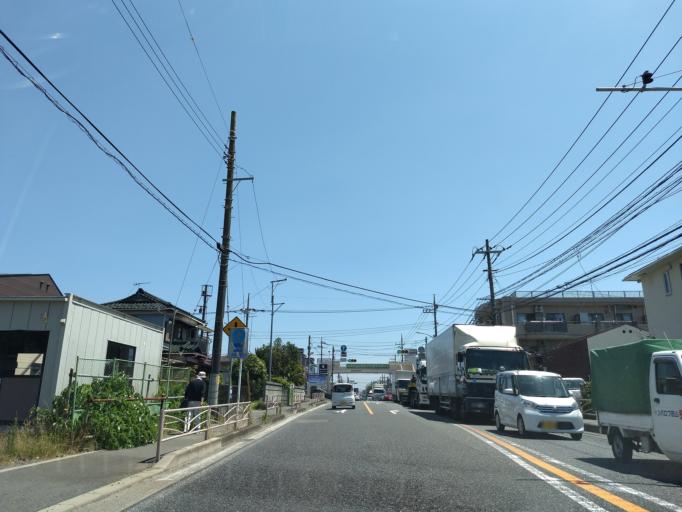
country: JP
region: Kanagawa
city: Isehara
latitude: 35.3942
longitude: 139.2875
